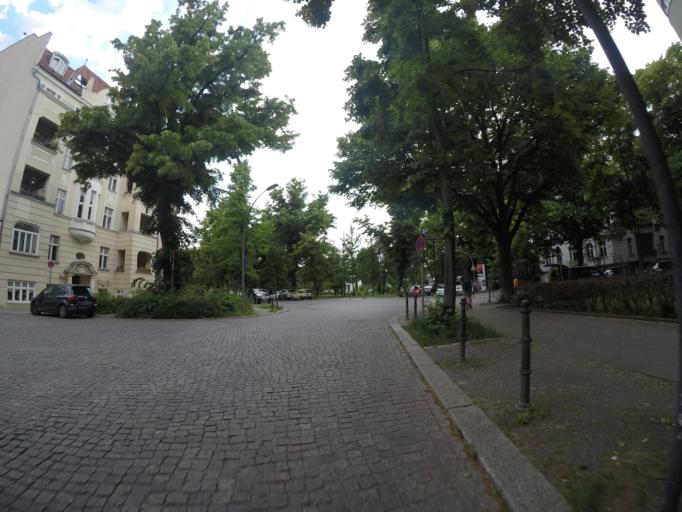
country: DE
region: Berlin
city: Schmargendorf
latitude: 52.4763
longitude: 13.2908
